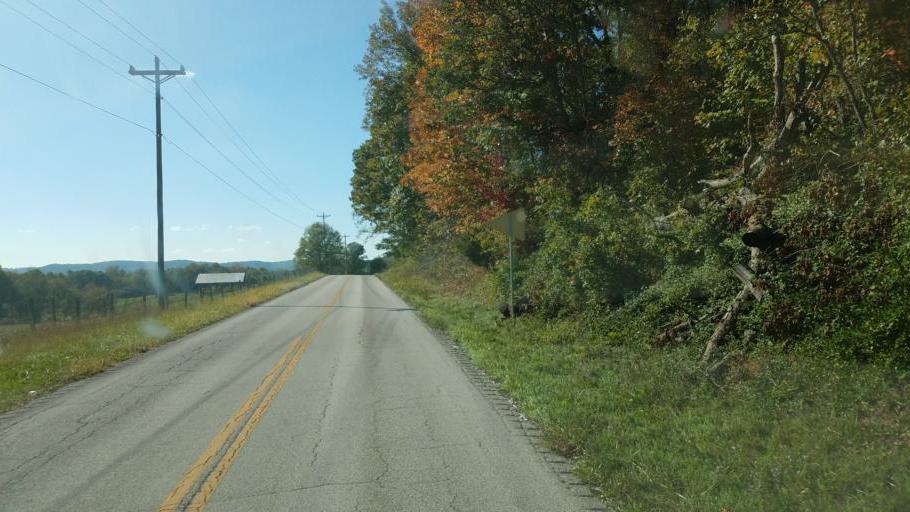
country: US
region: Kentucky
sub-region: Fleming County
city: Flemingsburg
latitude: 38.4683
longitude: -83.5454
